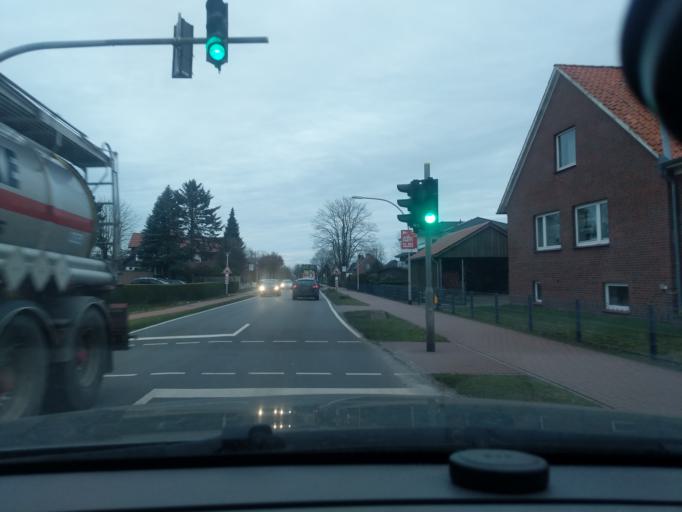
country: DE
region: Lower Saxony
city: Apensen
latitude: 53.4384
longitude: 9.6117
